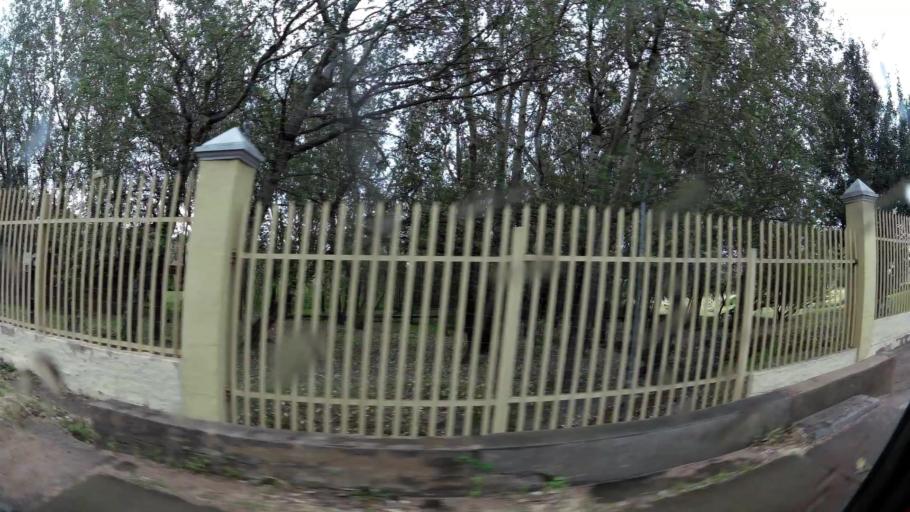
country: ZA
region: Gauteng
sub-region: City of Johannesburg Metropolitan Municipality
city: Roodepoort
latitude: -26.0972
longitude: 27.9213
